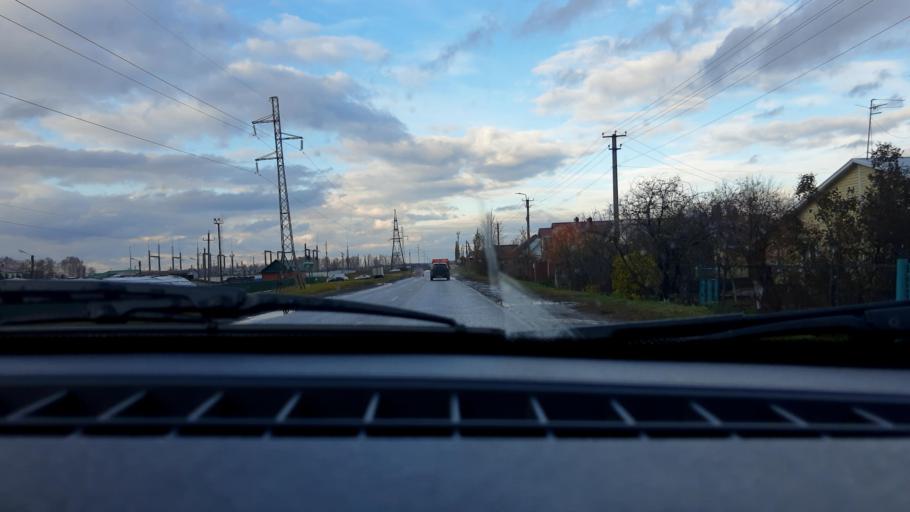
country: RU
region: Bashkortostan
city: Ufa
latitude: 54.8406
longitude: 55.9985
